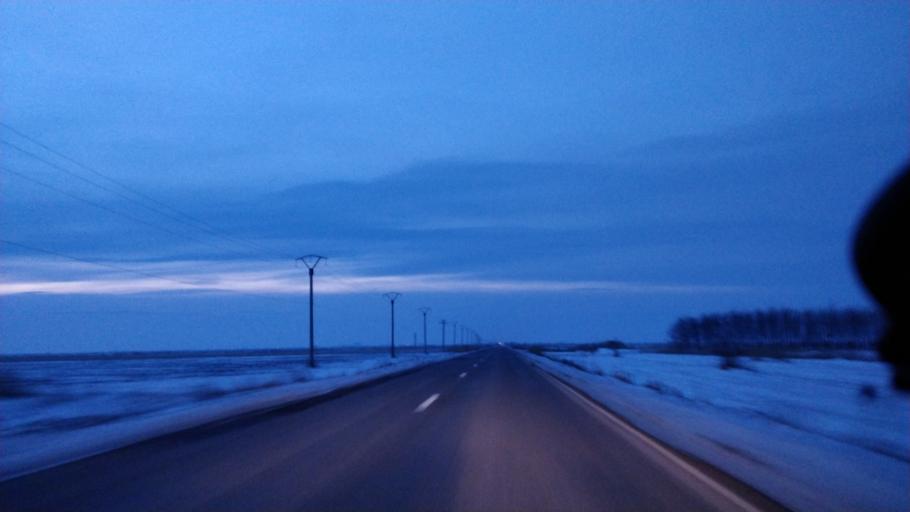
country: RO
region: Vrancea
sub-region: Comuna Vulturu
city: Vadu Rosca
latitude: 45.5966
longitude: 27.4665
